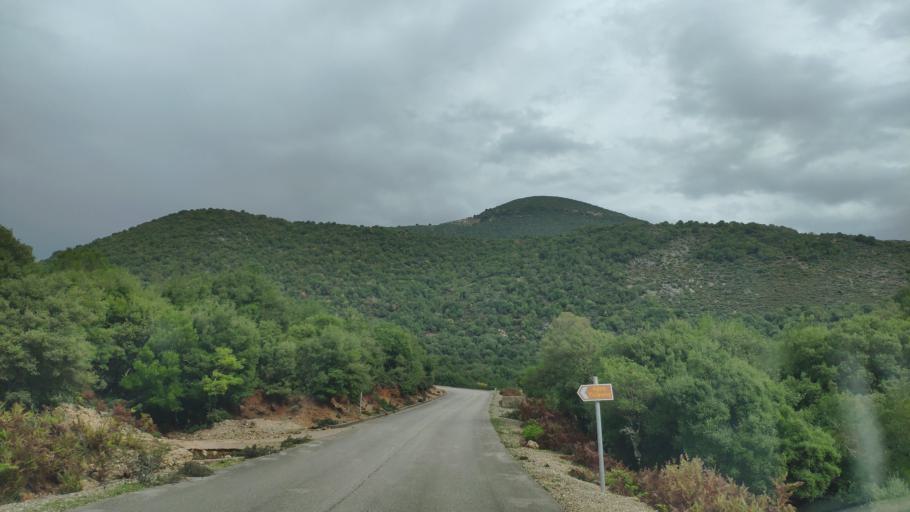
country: GR
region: Epirus
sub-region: Nomos Thesprotias
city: Paramythia
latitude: 39.4092
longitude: 20.6220
